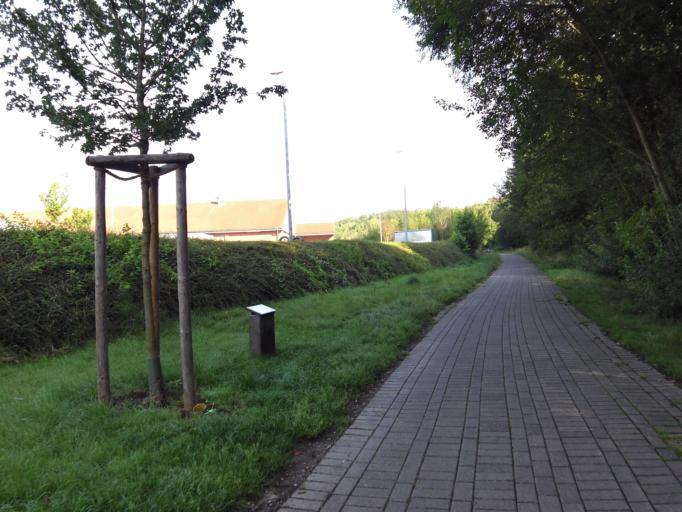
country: DE
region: North Rhine-Westphalia
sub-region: Regierungsbezirk Koln
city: Ubach-Palenberg
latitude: 50.9234
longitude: 6.1154
